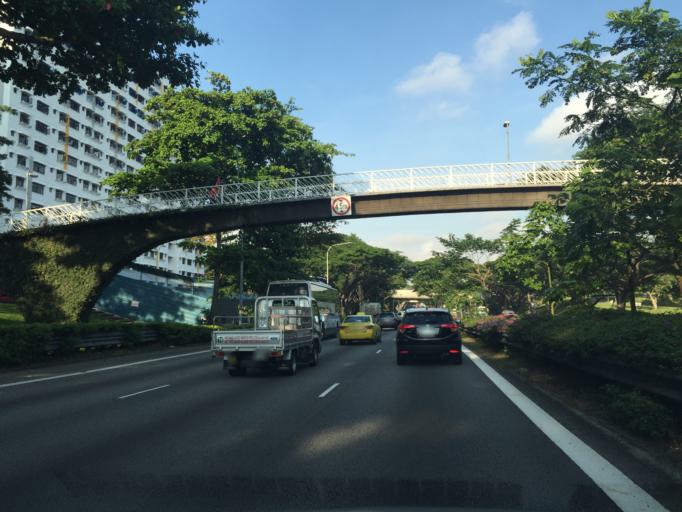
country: SG
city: Singapore
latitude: 1.3339
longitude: 103.9229
